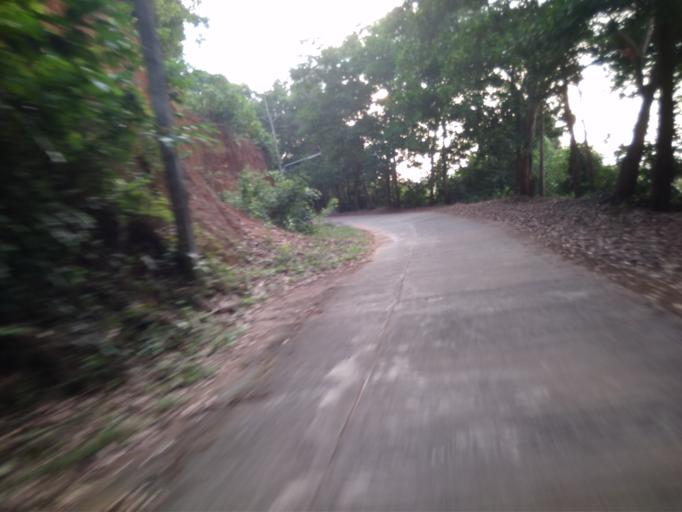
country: TH
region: Phangnga
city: Ko Yao
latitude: 8.1568
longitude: 98.6047
